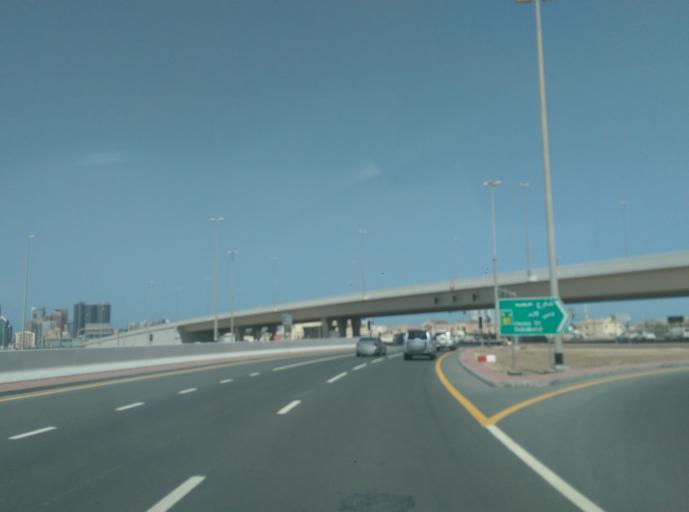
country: AE
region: Dubai
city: Dubai
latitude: 25.0837
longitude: 55.1980
